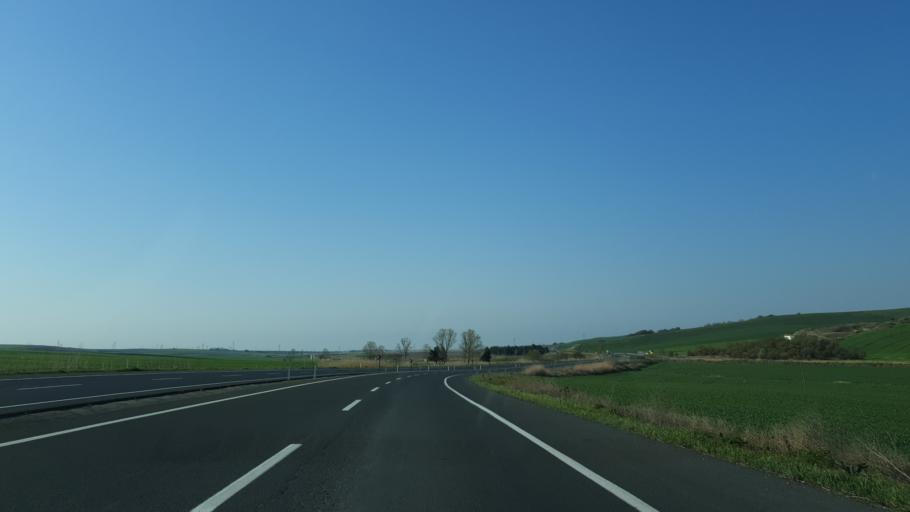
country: TR
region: Tekirdag
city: Corlu
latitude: 41.0547
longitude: 27.7376
